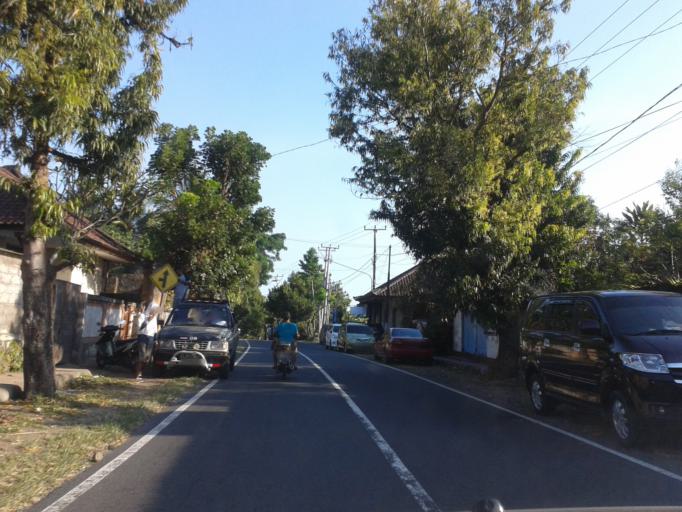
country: ID
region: Bali
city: Banjar Wangsian
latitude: -8.5001
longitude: 115.4035
